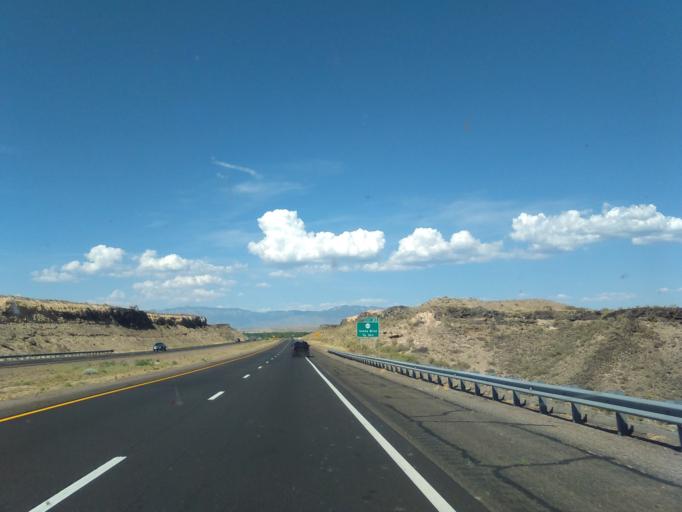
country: US
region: New Mexico
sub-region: Bernalillo County
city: South Valley
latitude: 34.9366
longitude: -106.7108
